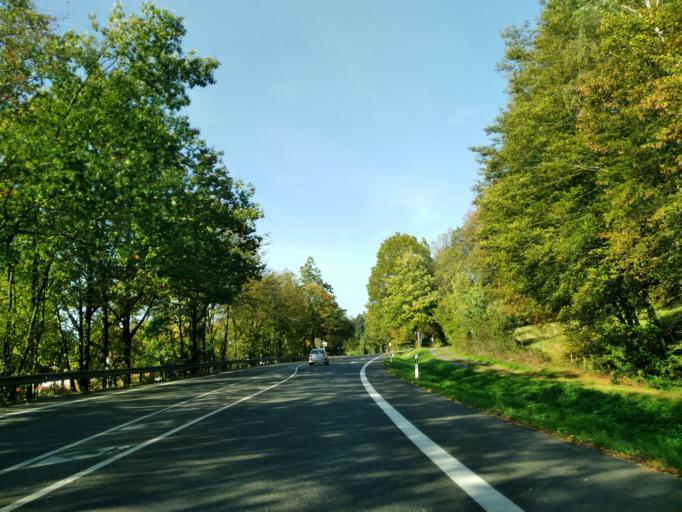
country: DE
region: North Rhine-Westphalia
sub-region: Regierungsbezirk Koln
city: Hennef
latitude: 50.7209
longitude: 7.2764
